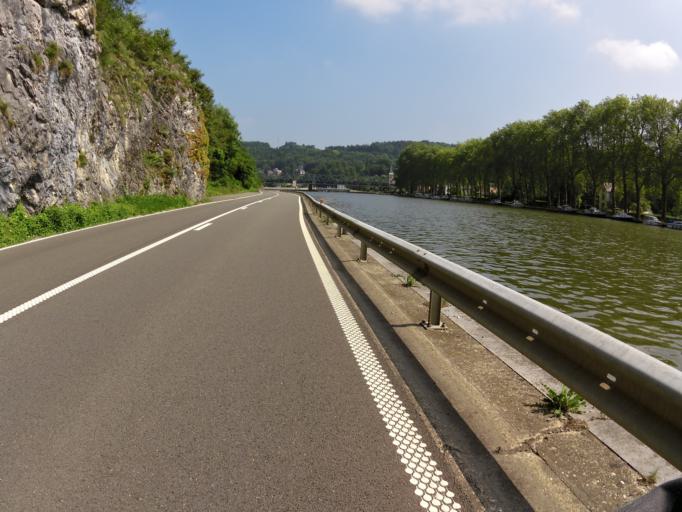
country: BE
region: Wallonia
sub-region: Province de Namur
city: Dinant
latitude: 50.2416
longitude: 4.9009
